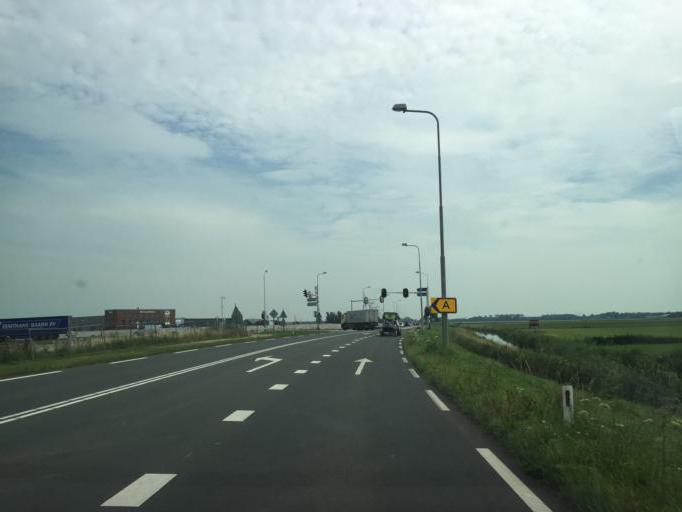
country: NL
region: North Holland
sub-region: Gemeente Opmeer
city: Opmeer
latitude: 52.6211
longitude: 4.9660
